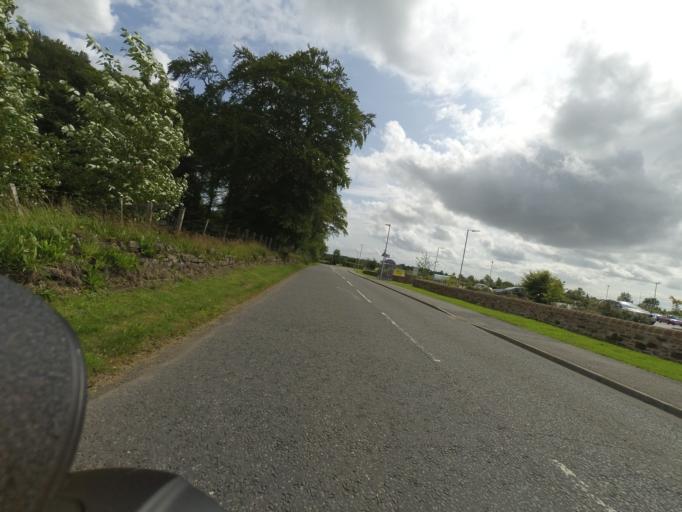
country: GB
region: Scotland
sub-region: Highland
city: Tain
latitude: 57.8044
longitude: -4.0460
